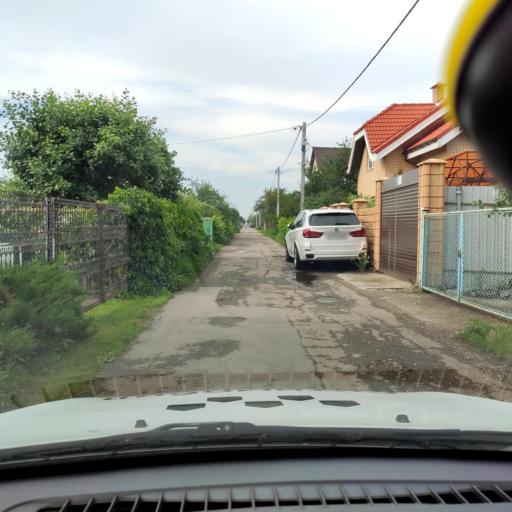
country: RU
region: Samara
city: Podstepki
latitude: 53.5763
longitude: 49.0789
